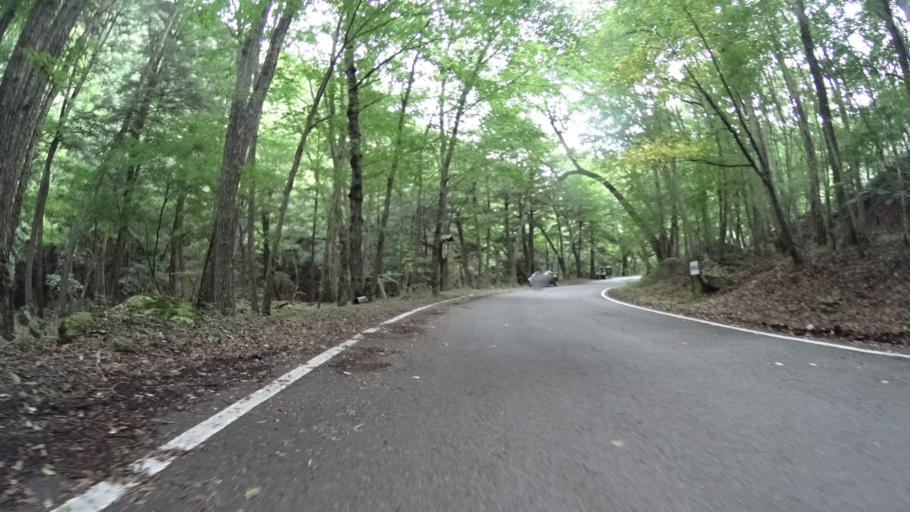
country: JP
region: Yamanashi
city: Nirasaki
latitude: 35.8593
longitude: 138.5628
